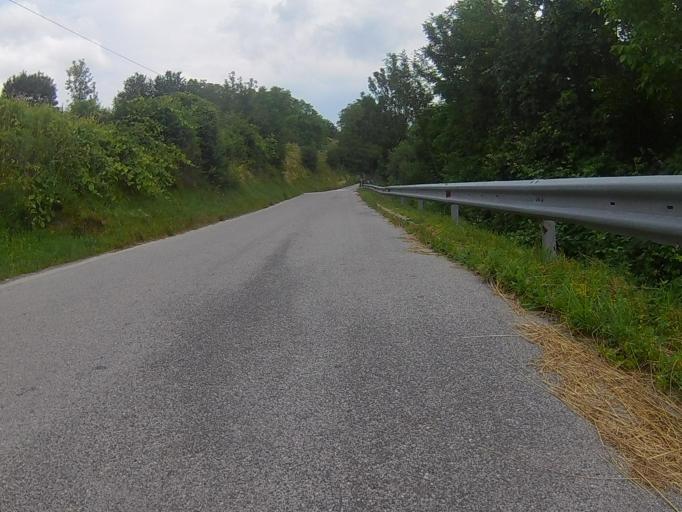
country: SI
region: Sentilj
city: Sentilj v Slov. Goricah
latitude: 46.6718
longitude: 15.6314
